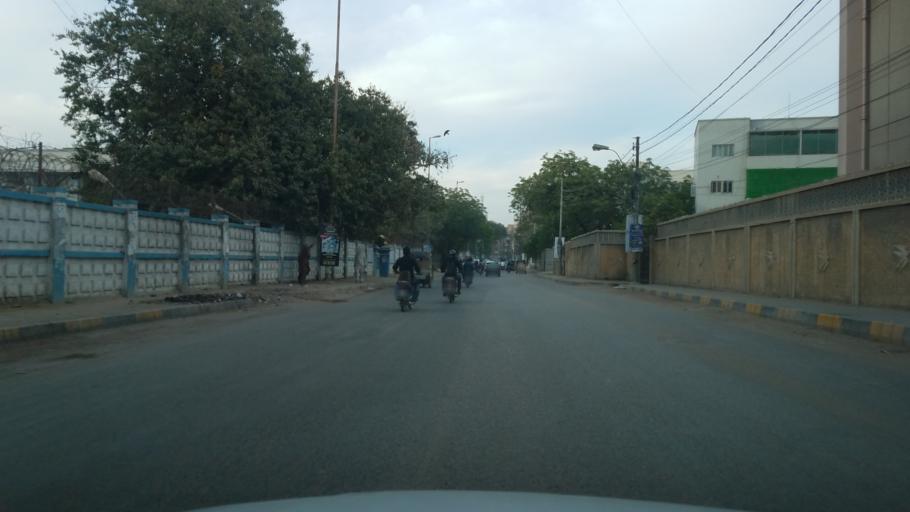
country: PK
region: Sindh
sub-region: Karachi District
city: Karachi
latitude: 24.8710
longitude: 67.0281
